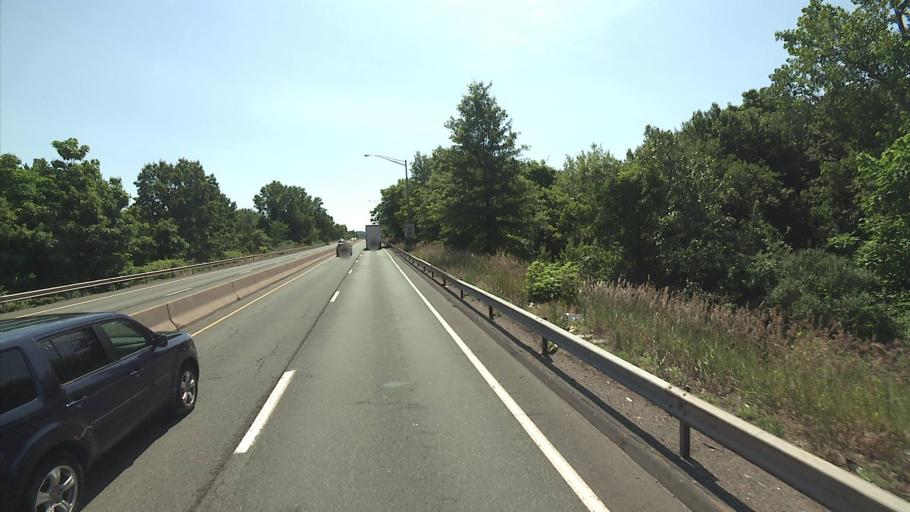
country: US
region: Connecticut
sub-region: Hartford County
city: Plainville
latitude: 41.6781
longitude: -72.8695
